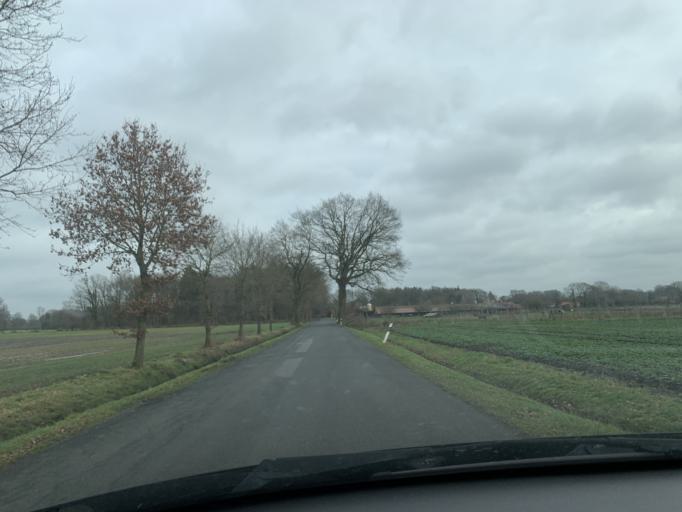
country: DE
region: Lower Saxony
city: Wiefelstede
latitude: 53.1985
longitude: 8.1153
